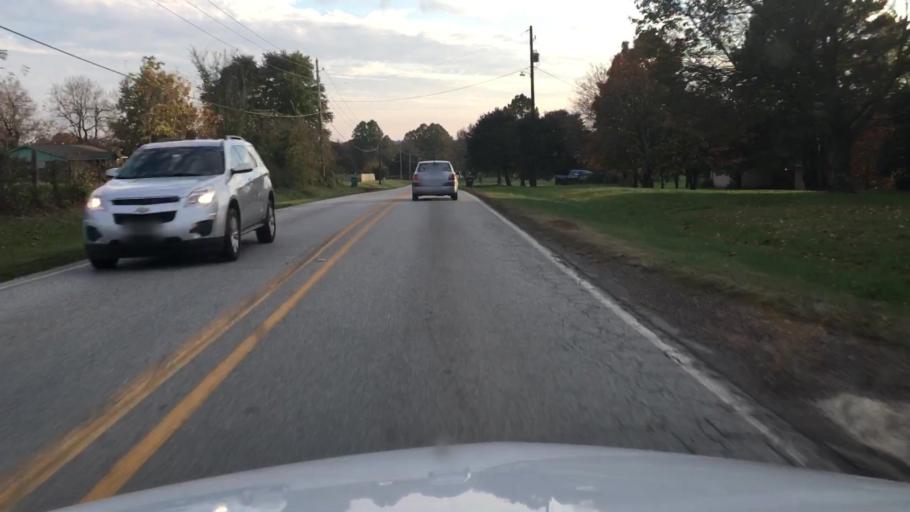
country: US
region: Arkansas
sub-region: Washington County
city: Elm Springs
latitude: 36.2196
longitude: -94.2305
